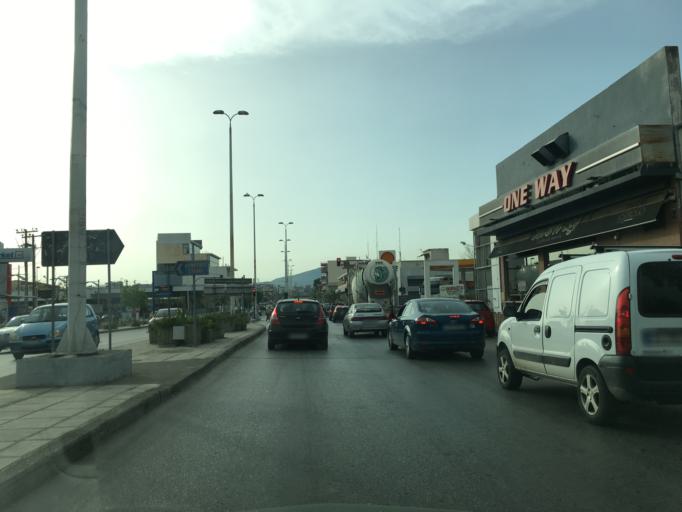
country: GR
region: Thessaly
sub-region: Nomos Magnisias
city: Nea Ionia
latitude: 39.3632
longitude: 22.9308
